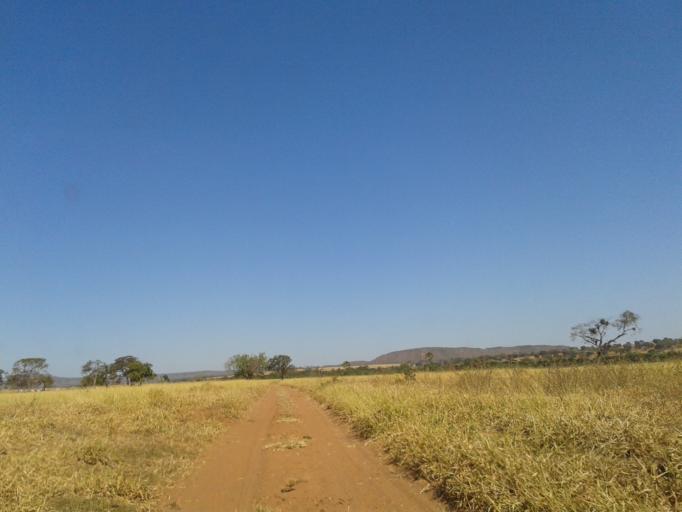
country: BR
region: Minas Gerais
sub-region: Santa Vitoria
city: Santa Vitoria
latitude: -19.1550
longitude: -50.0274
